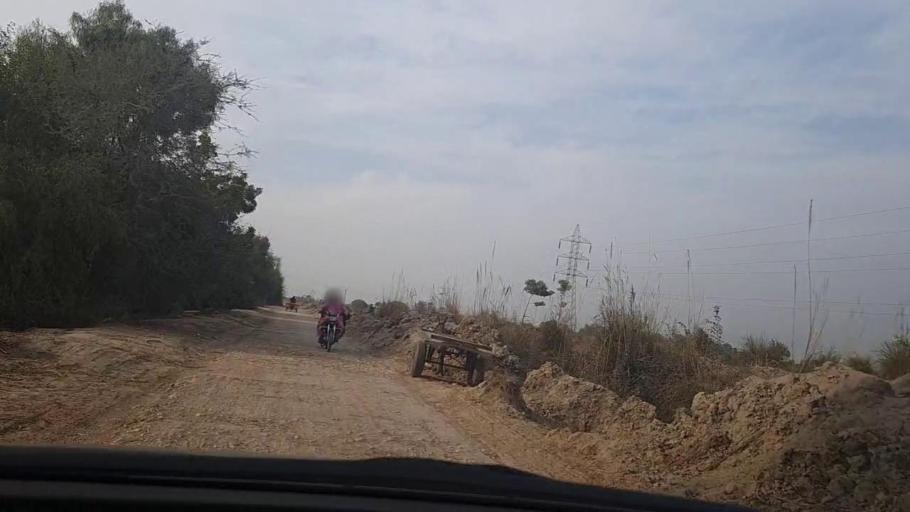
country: PK
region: Sindh
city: Daulatpur
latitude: 26.3324
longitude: 68.0775
